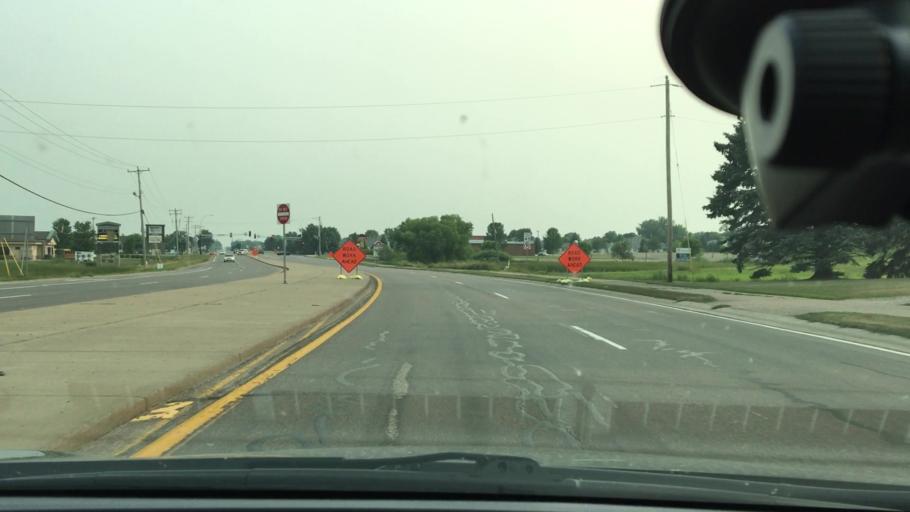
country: US
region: Minnesota
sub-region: Wright County
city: Albertville
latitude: 45.2373
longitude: -93.6641
